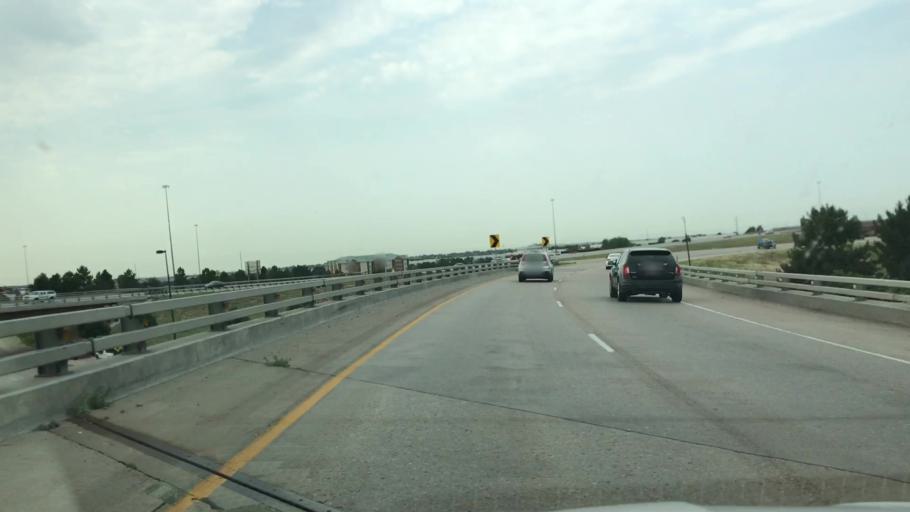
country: US
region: Colorado
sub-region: Adams County
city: Aurora
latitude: 39.7709
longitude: -104.7917
